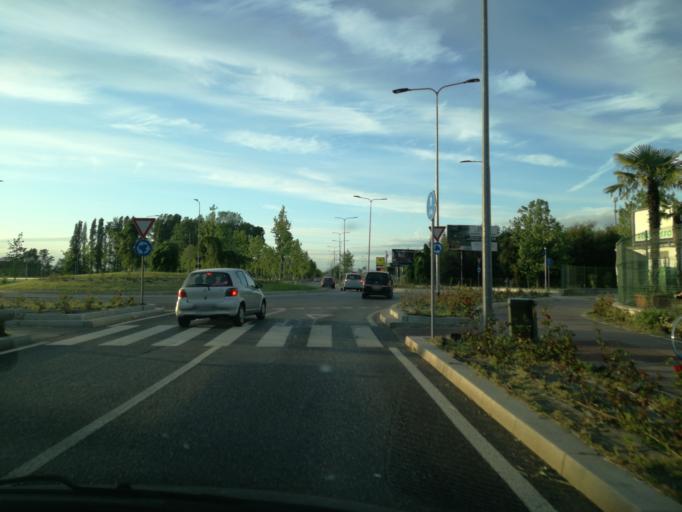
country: IT
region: Lombardy
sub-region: Citta metropolitana di Milano
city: Noverasco-Sporting Mirasole
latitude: 45.4066
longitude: 9.2082
